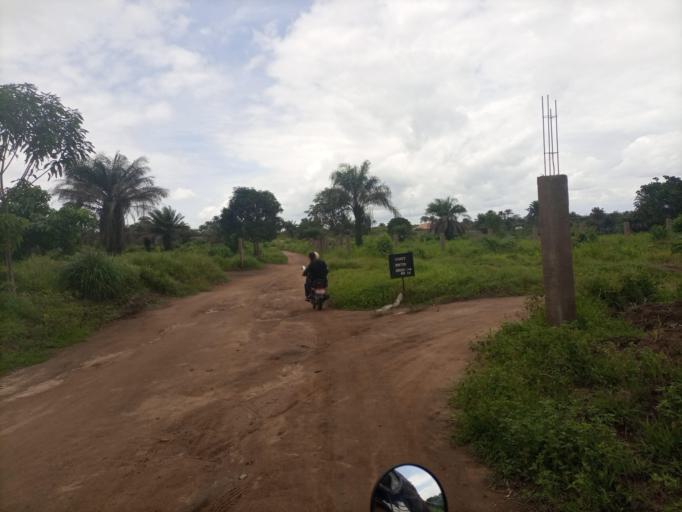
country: SL
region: Northern Province
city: Masoyila
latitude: 8.5690
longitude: -13.1586
